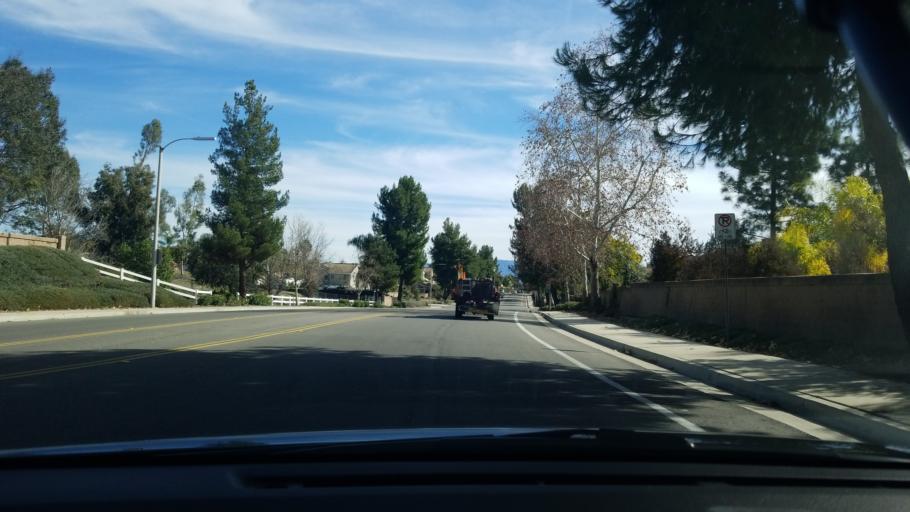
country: US
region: California
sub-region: Riverside County
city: Murrieta Hot Springs
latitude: 33.5727
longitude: -117.1702
